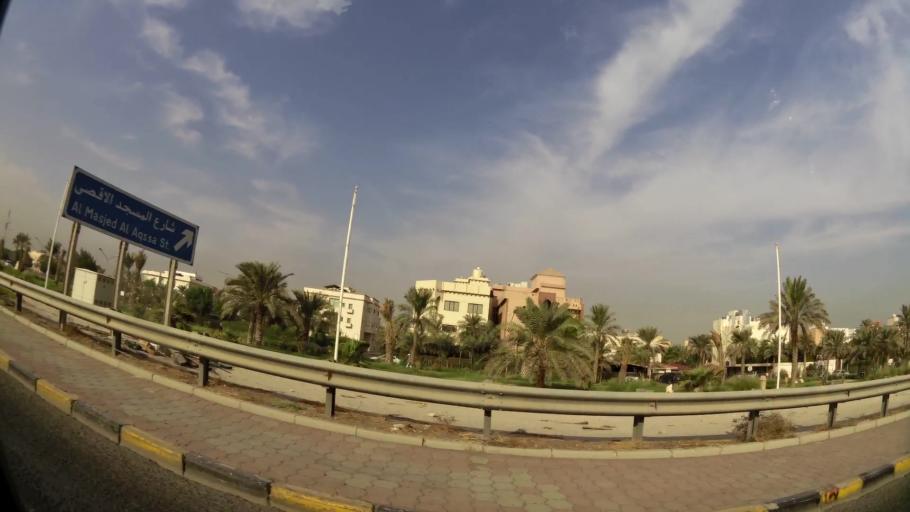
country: KW
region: Muhafazat Hawalli
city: Ar Rumaythiyah
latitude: 29.3102
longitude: 48.0861
